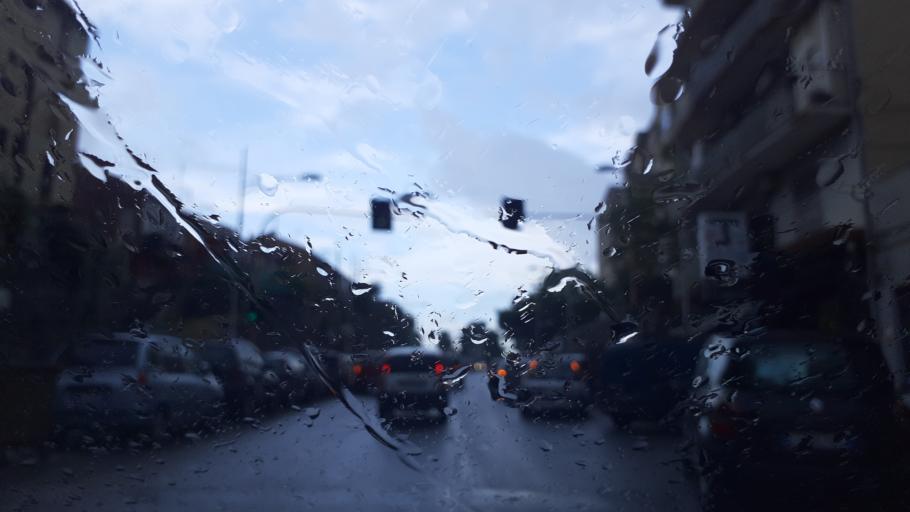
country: IT
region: Sicily
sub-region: Catania
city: Catania
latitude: 37.5014
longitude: 15.0668
